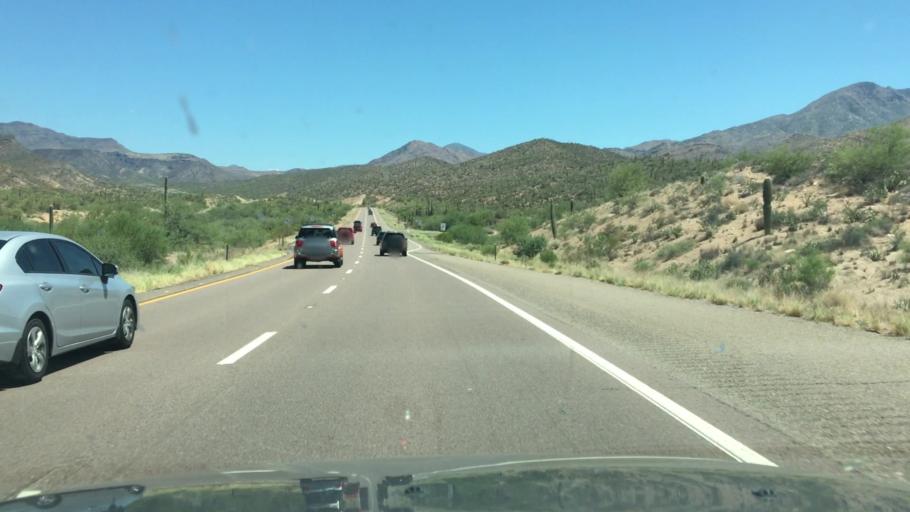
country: US
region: Arizona
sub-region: Maricopa County
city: Rio Verde
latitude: 33.7530
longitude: -111.4975
